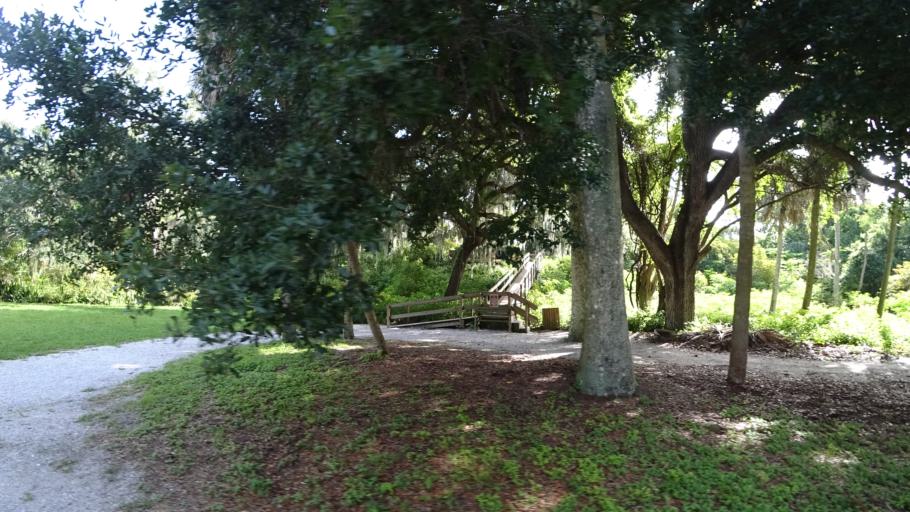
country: US
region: Florida
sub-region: Manatee County
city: West Bradenton
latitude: 27.5307
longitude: -82.6267
